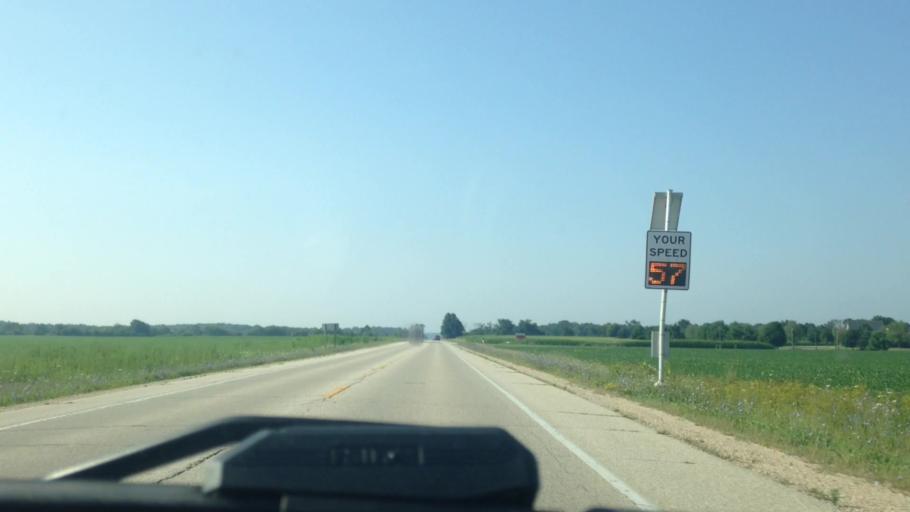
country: US
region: Wisconsin
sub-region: Washington County
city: Richfield
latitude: 43.2210
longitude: -88.2618
